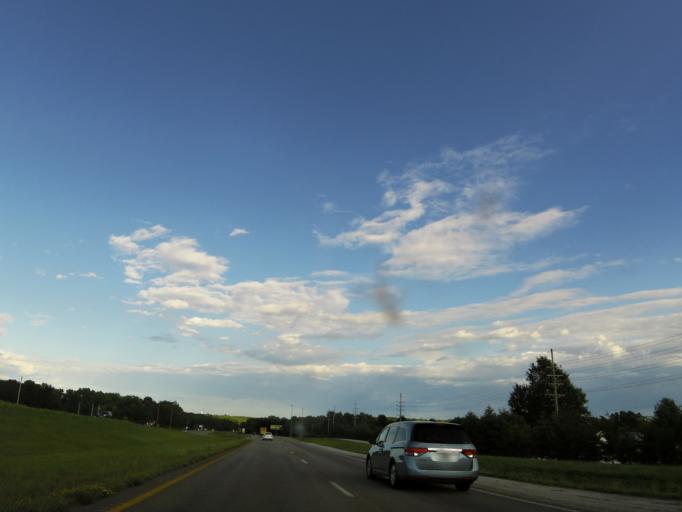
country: US
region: Missouri
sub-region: Saint Charles County
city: Wentzville
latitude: 38.8648
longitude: -90.8841
